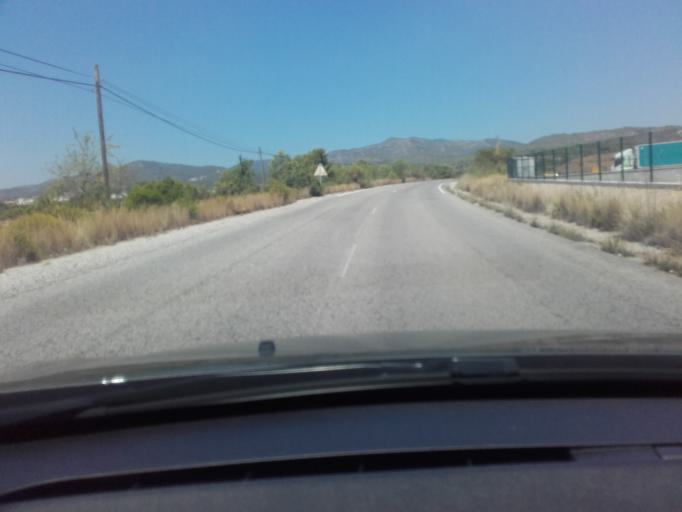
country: ES
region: Catalonia
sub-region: Provincia de Tarragona
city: la Bisbal del Penedes
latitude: 41.2707
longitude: 1.5036
